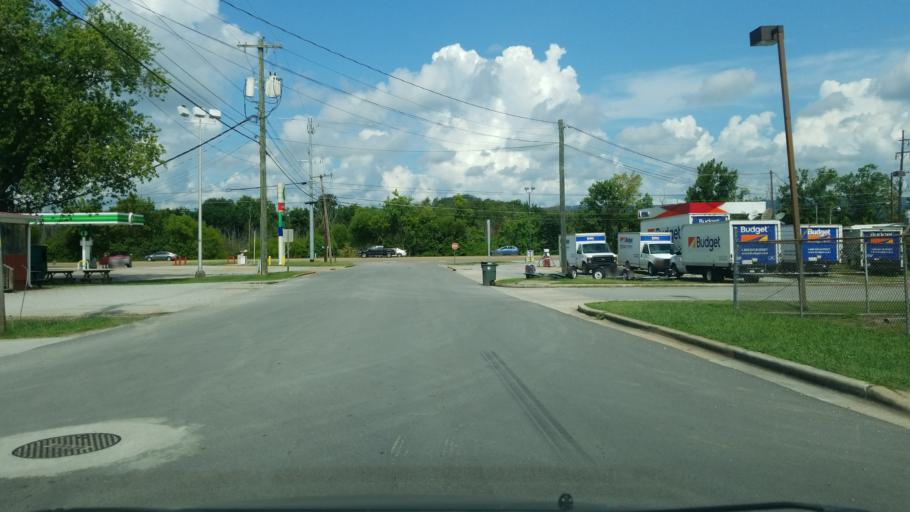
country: US
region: Tennessee
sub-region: Hamilton County
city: East Chattanooga
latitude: 35.0728
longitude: -85.2674
